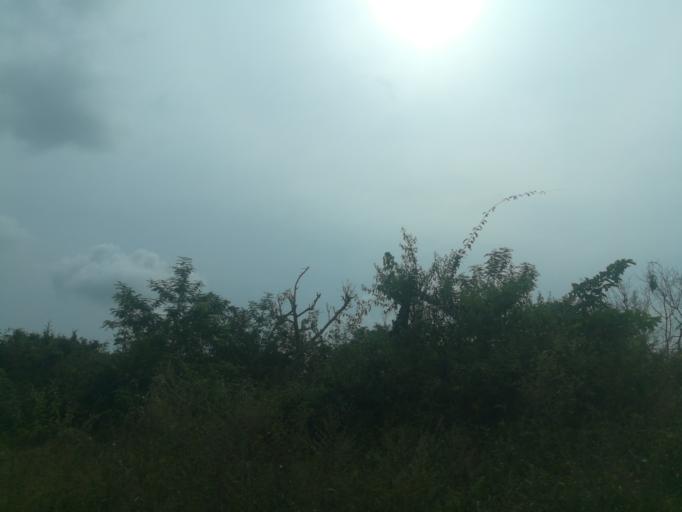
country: NG
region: Ogun
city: Ayetoro
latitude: 7.2789
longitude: 3.0941
